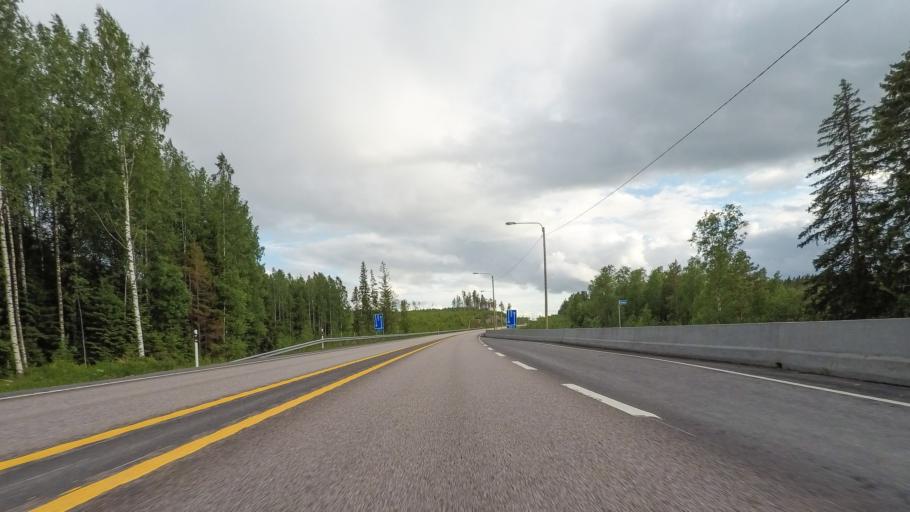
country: FI
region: Paijanne Tavastia
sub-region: Lahti
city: Heinola
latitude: 61.3728
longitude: 26.0511
